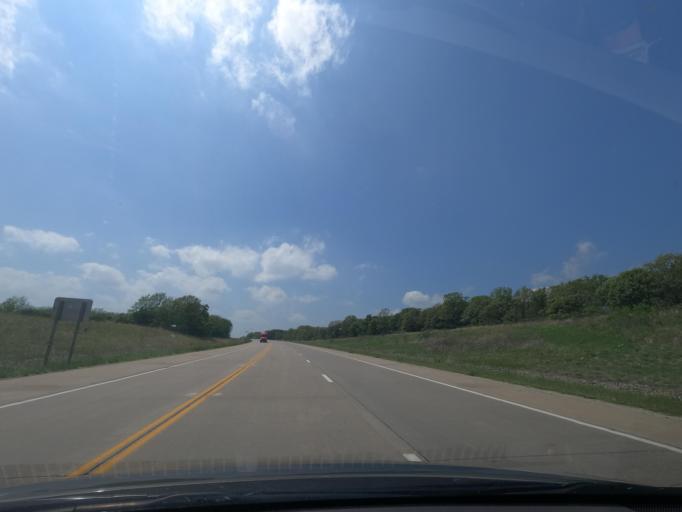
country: US
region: Kansas
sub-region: Wilson County
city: Fredonia
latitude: 37.6138
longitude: -95.9006
